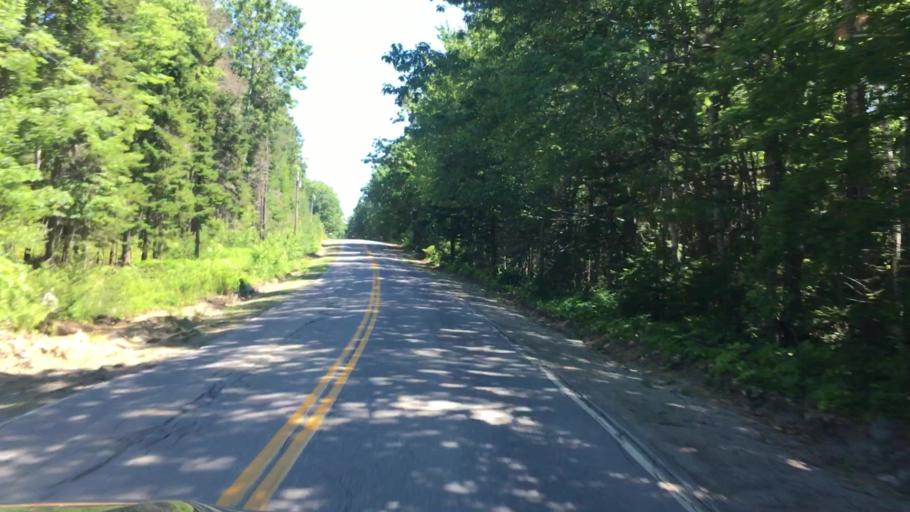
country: US
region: Maine
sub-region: Hancock County
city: Penobscot
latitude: 44.4401
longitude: -68.7076
